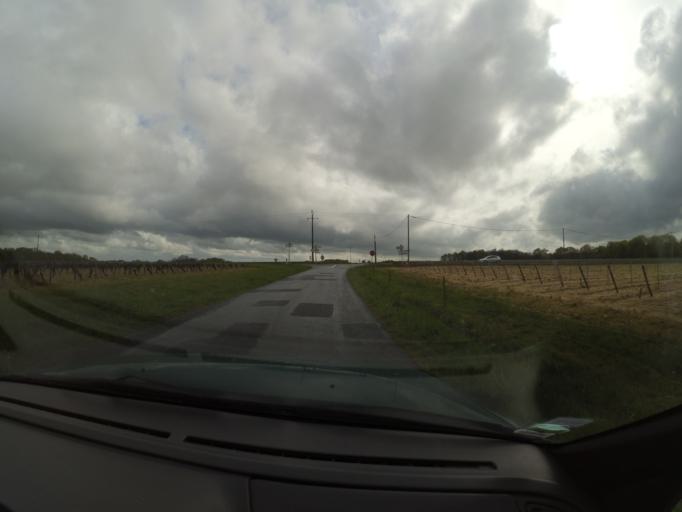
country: FR
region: Pays de la Loire
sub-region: Departement de la Loire-Atlantique
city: Monnieres
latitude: 47.1179
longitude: -1.3604
